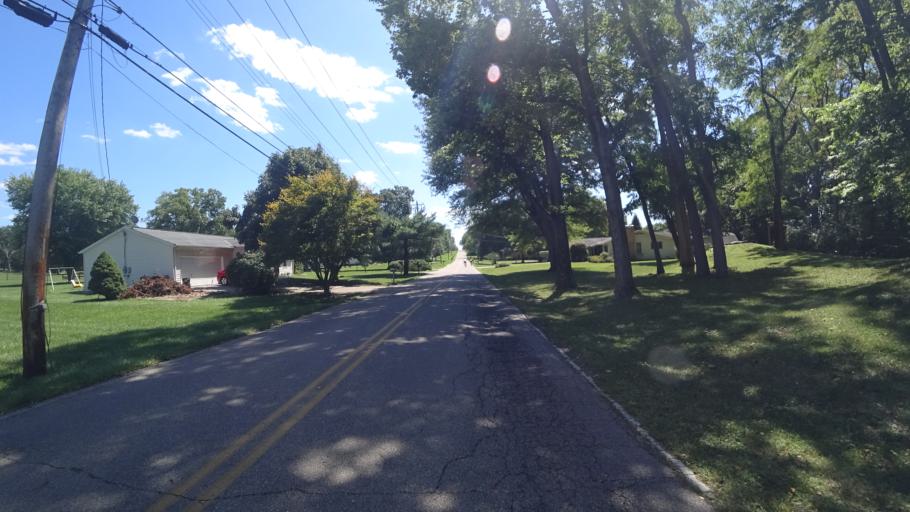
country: US
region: Ohio
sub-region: Butler County
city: New Miami
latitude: 39.4115
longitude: -84.5278
